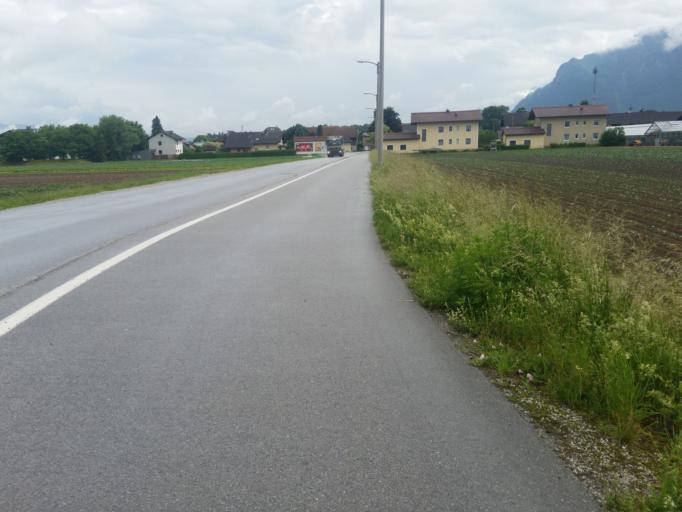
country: DE
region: Bavaria
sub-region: Upper Bavaria
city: Ainring
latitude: 47.7910
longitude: 12.9932
